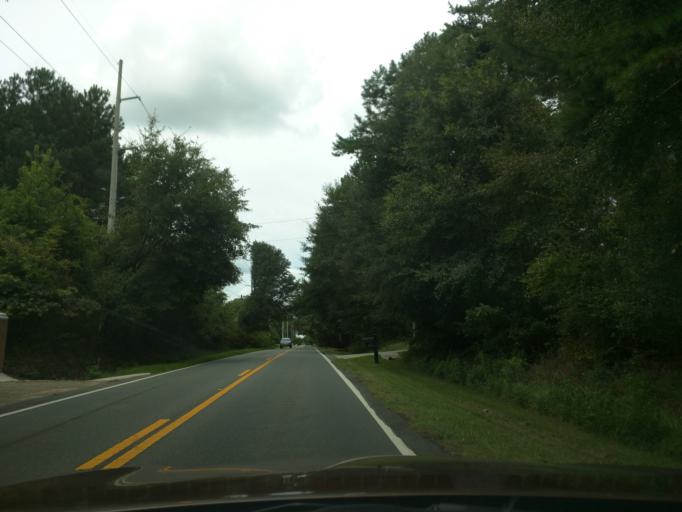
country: US
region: Florida
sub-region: Leon County
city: Tallahassee
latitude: 30.5598
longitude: -84.1894
